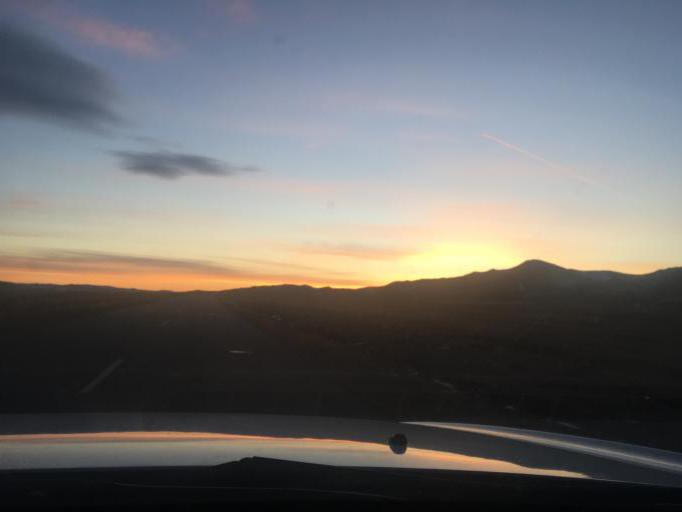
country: MN
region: Central Aimak
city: Mandal
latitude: 48.0941
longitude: 106.6088
